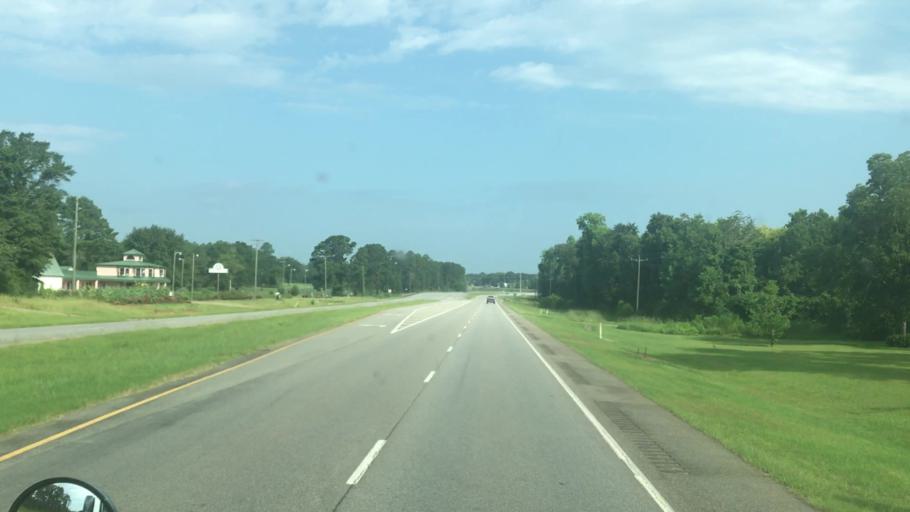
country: US
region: Georgia
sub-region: Early County
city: Blakely
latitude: 31.3523
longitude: -84.9183
